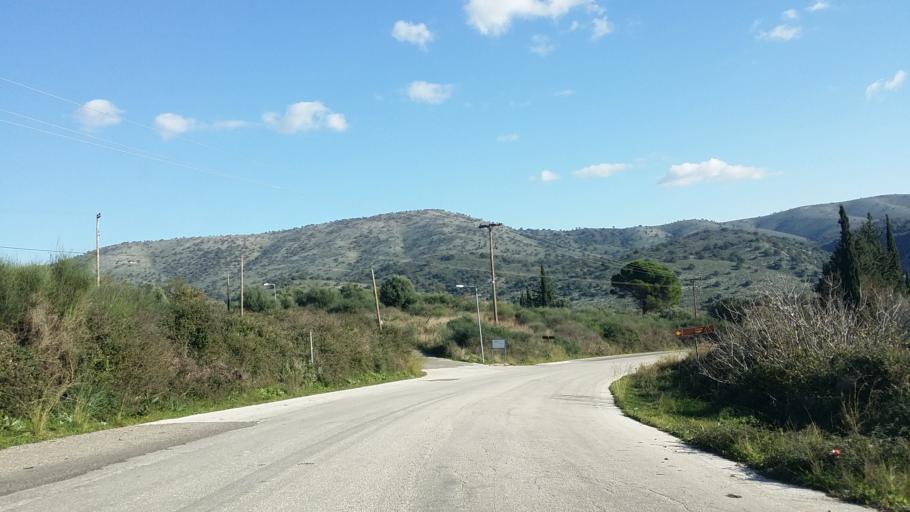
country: GR
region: West Greece
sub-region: Nomos Aitolias kai Akarnanias
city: Astakos
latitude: 38.5415
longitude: 21.0860
